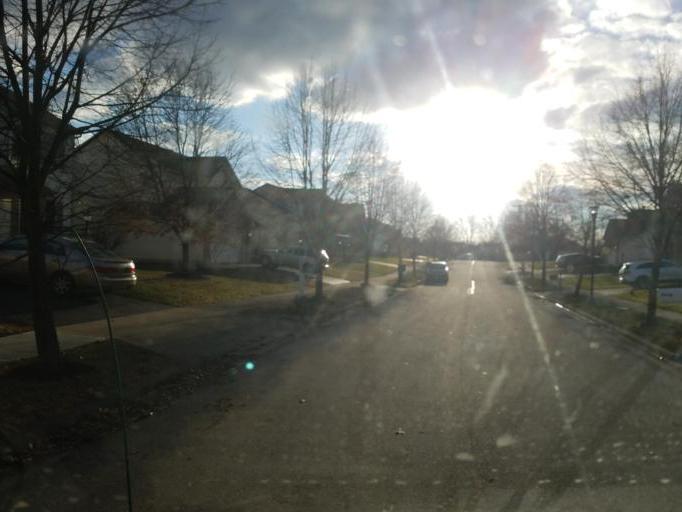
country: US
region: Ohio
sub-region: Delaware County
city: Delaware
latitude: 40.3126
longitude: -83.1050
